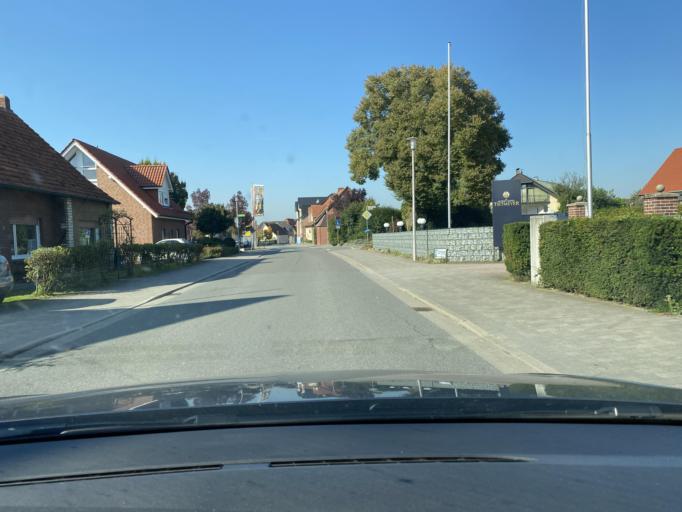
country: DE
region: North Rhine-Westphalia
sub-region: Regierungsbezirk Munster
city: Schoppingen
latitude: 52.0901
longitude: 7.2420
